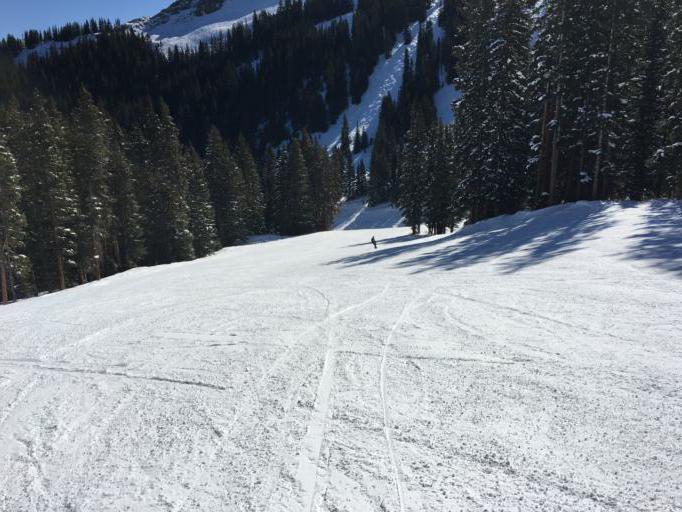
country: US
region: Colorado
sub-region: Summit County
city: Frisco
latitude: 39.4779
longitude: -106.1656
